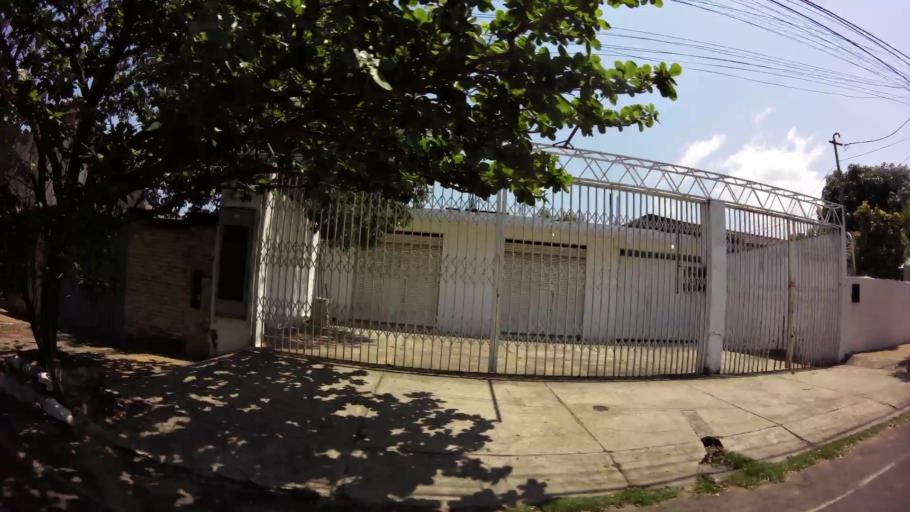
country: PY
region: Asuncion
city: Asuncion
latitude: -25.3044
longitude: -57.6475
